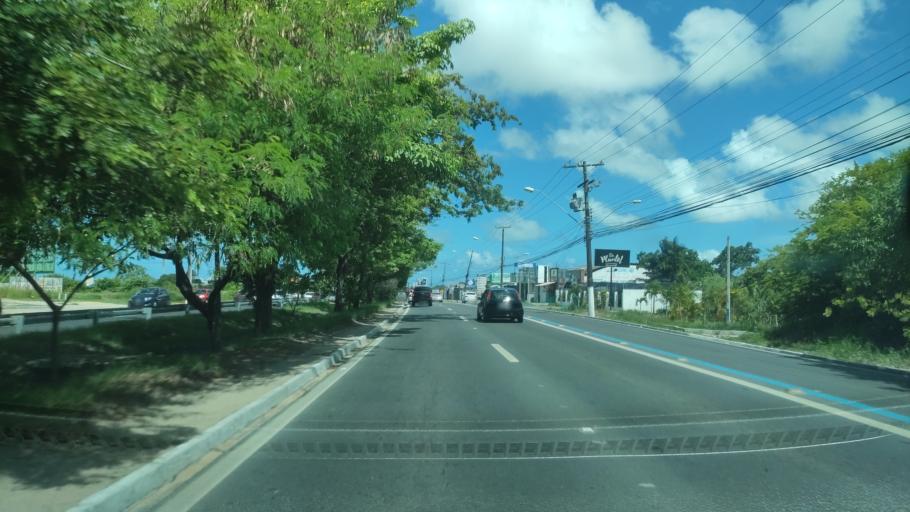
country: BR
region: Alagoas
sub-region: Maceio
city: Maceio
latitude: -9.5976
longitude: -35.7506
